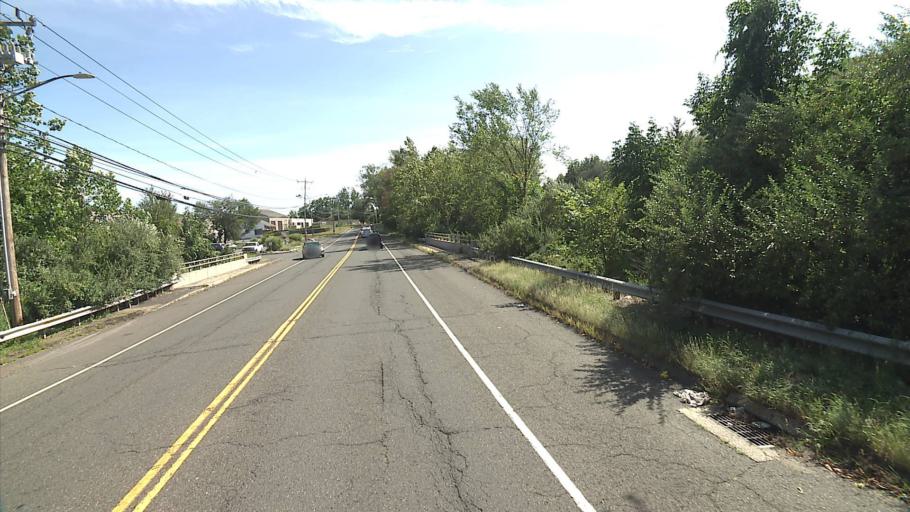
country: US
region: Connecticut
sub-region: New Haven County
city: Cheshire Village
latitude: 41.5273
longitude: -72.9327
